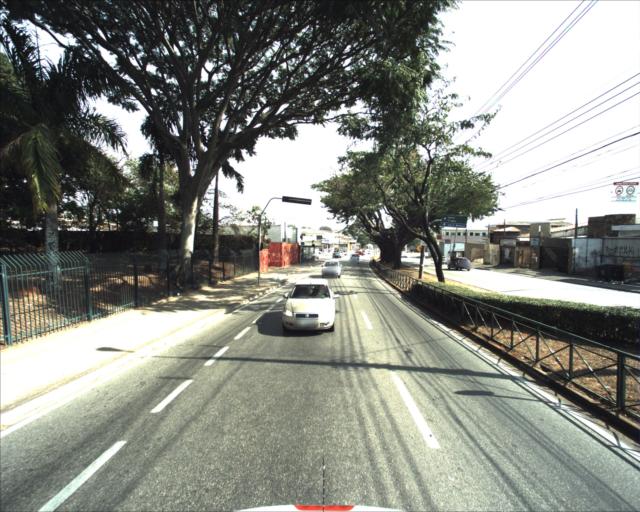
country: BR
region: Sao Paulo
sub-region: Sorocaba
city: Sorocaba
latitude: -23.4846
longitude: -47.4703
